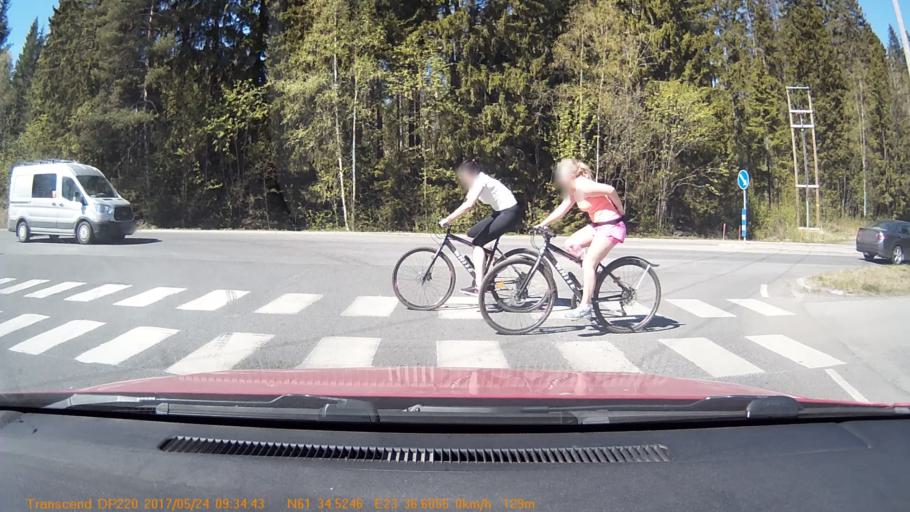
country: FI
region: Pirkanmaa
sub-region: Tampere
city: Yloejaervi
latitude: 61.5754
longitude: 23.6103
